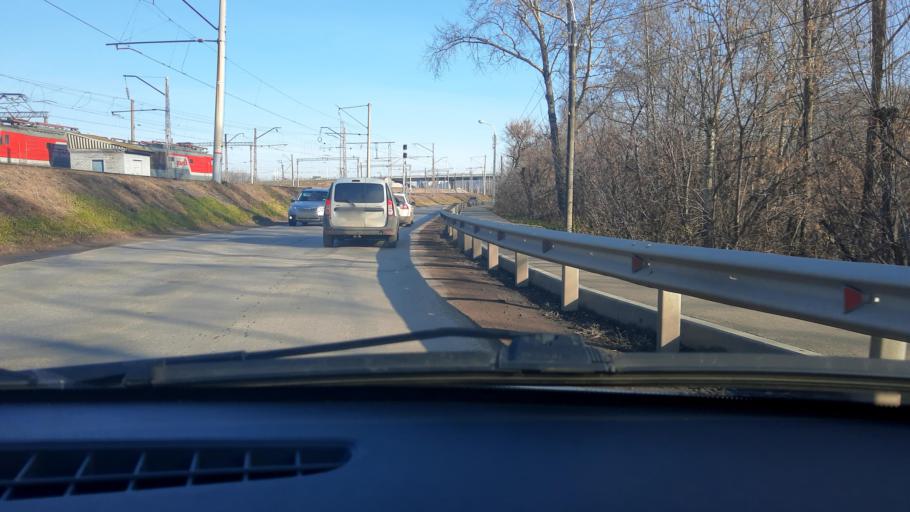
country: RU
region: Bashkortostan
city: Mikhaylovka
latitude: 54.7014
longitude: 55.8504
